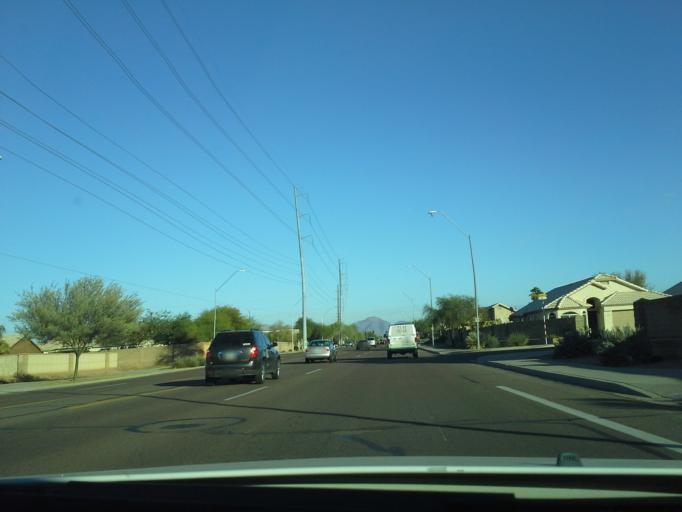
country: US
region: Arizona
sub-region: Maricopa County
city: Paradise Valley
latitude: 33.6551
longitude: -112.0181
